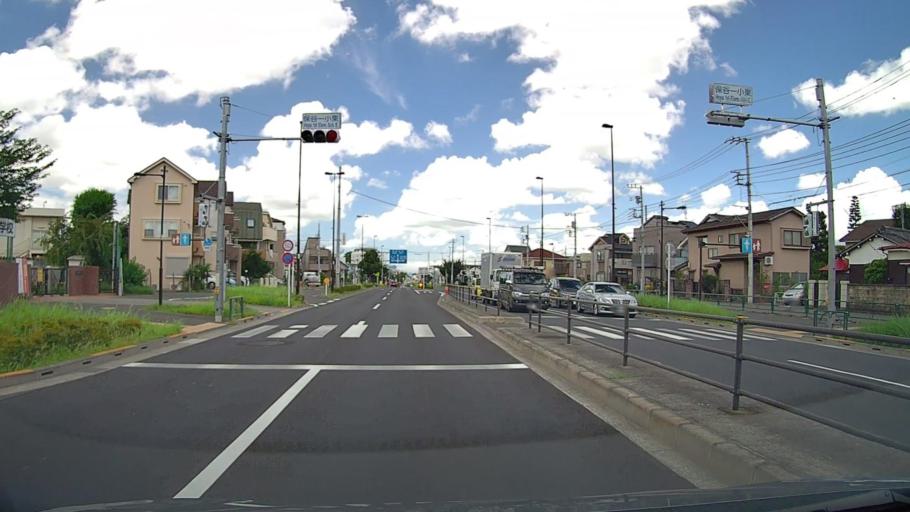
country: JP
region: Tokyo
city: Tanashicho
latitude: 35.7492
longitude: 139.5588
